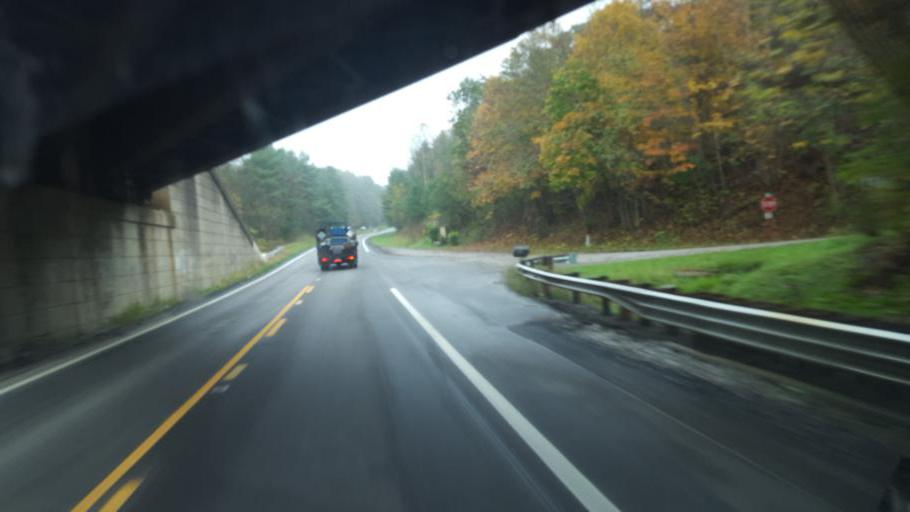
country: US
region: Ohio
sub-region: Tuscarawas County
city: Rockford
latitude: 40.4129
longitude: -81.2240
